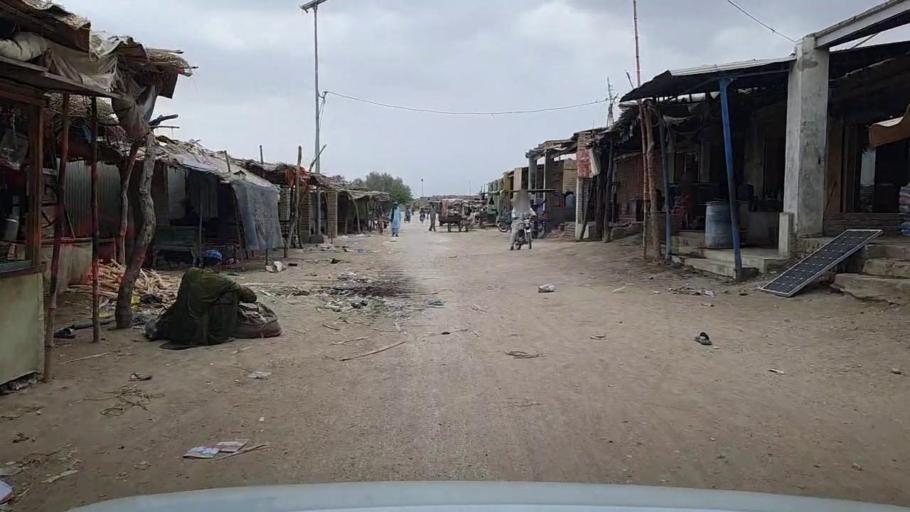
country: PK
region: Sindh
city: Sehwan
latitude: 26.3404
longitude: 67.7213
